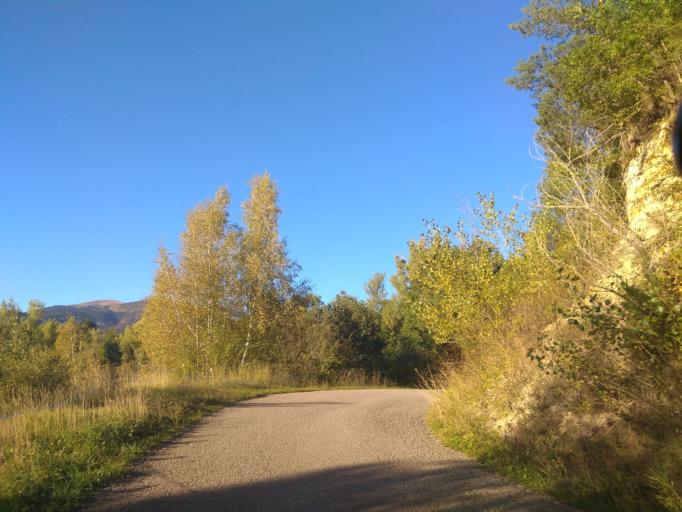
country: ES
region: Catalonia
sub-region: Provincia de Lleida
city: Lles de Cerdanya
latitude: 42.3540
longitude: 1.7269
